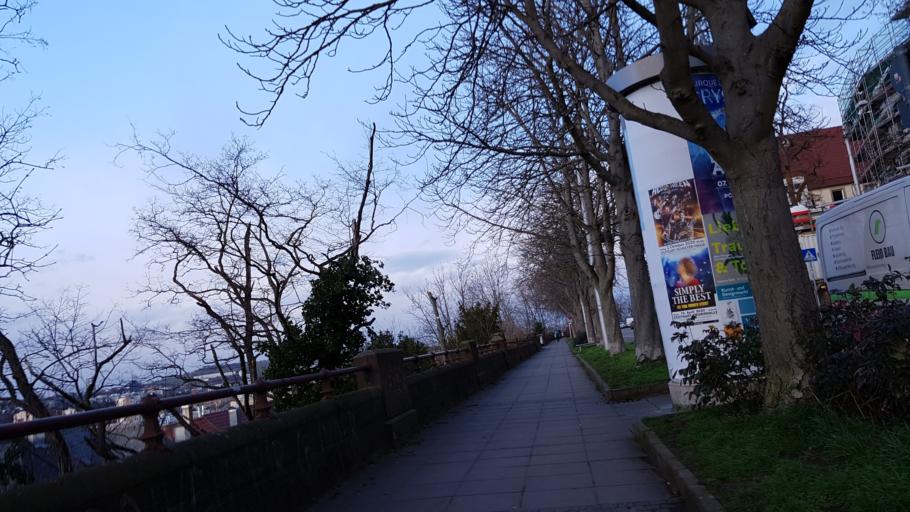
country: DE
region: Baden-Wuerttemberg
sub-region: Regierungsbezirk Stuttgart
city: Stuttgart
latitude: 48.7820
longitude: 9.1921
